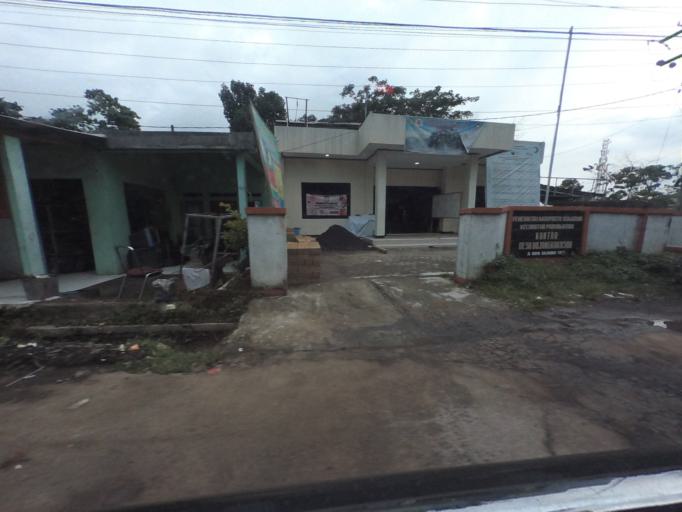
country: ID
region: West Java
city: Cicurug
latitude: -6.8344
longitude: 106.7606
